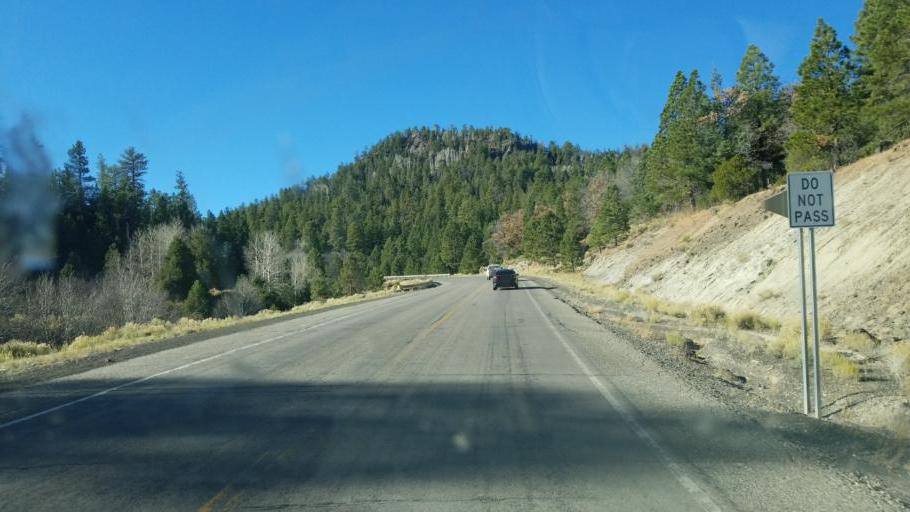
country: US
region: New Mexico
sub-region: McKinley County
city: Navajo
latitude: 36.0970
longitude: -108.8586
